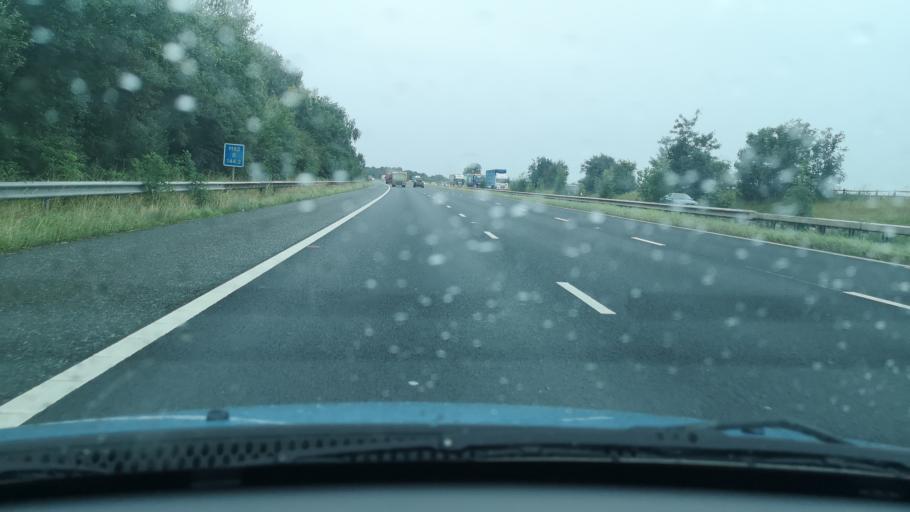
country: GB
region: England
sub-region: East Riding of Yorkshire
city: Pollington
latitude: 53.6939
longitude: -1.1235
